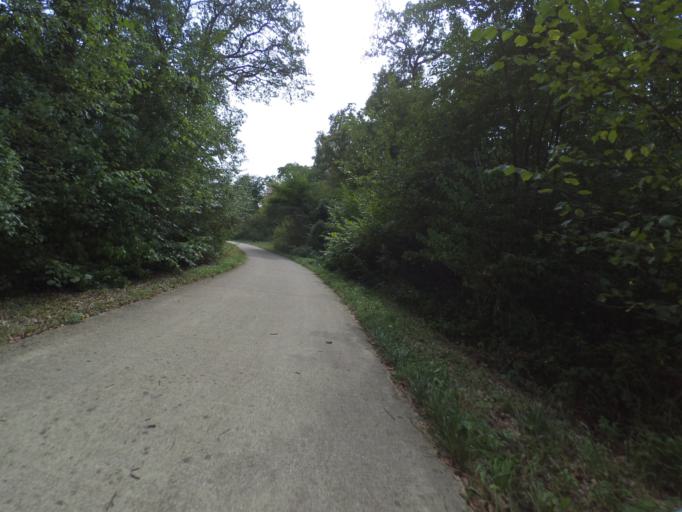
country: LU
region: Grevenmacher
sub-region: Canton de Remich
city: Bous
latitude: 49.5267
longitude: 6.3187
